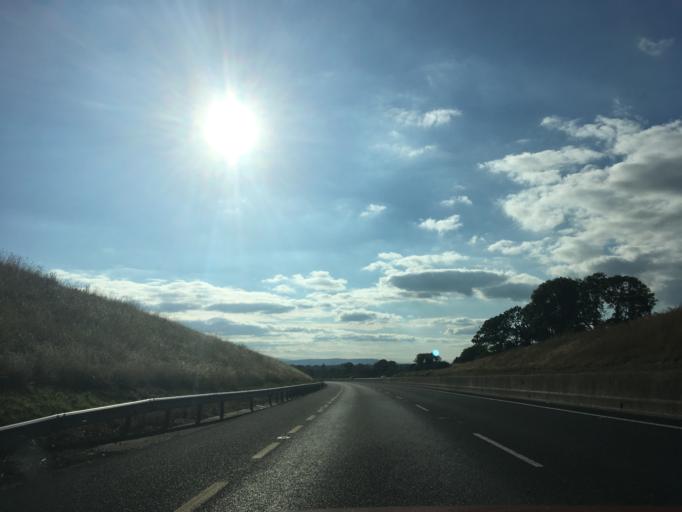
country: IE
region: Munster
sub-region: Waterford
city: Waterford
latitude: 52.2896
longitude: -7.1047
